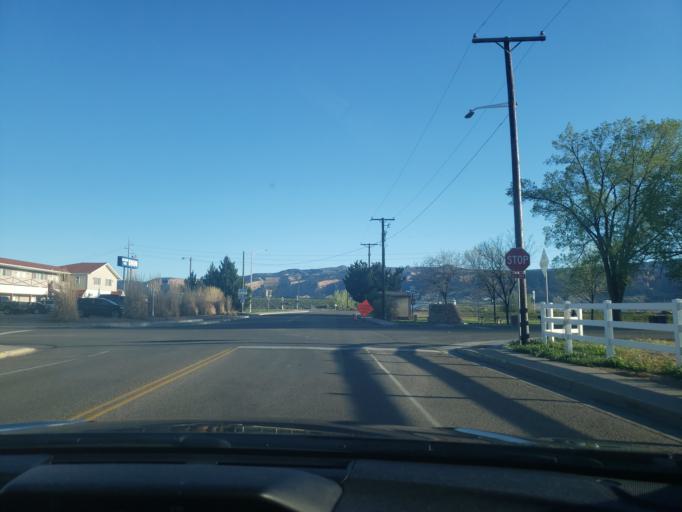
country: US
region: Colorado
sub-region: Mesa County
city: Fruita
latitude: 39.1591
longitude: -108.7384
